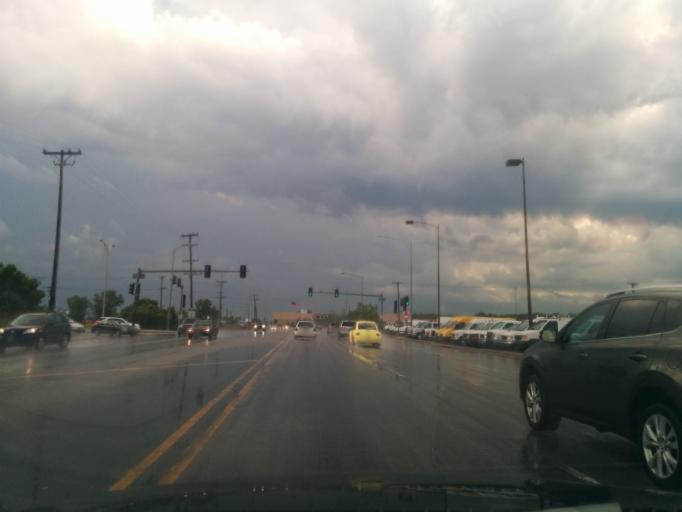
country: US
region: Illinois
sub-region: Cook County
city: Summit
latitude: 41.7750
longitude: -87.8022
